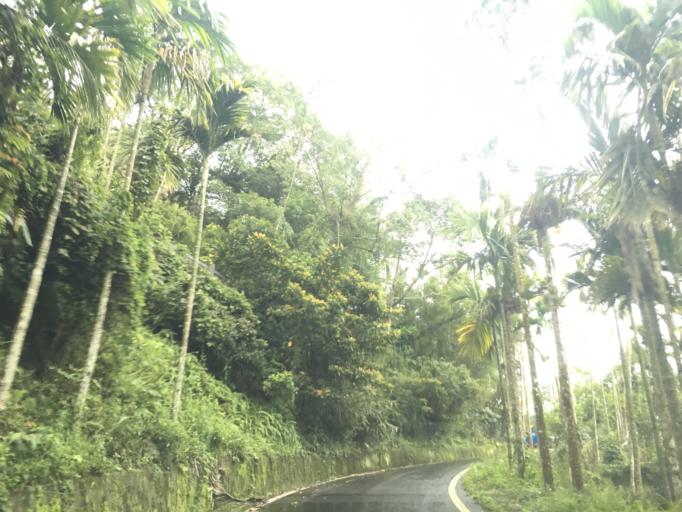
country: TW
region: Taiwan
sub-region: Yunlin
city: Douliu
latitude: 23.5590
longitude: 120.6553
